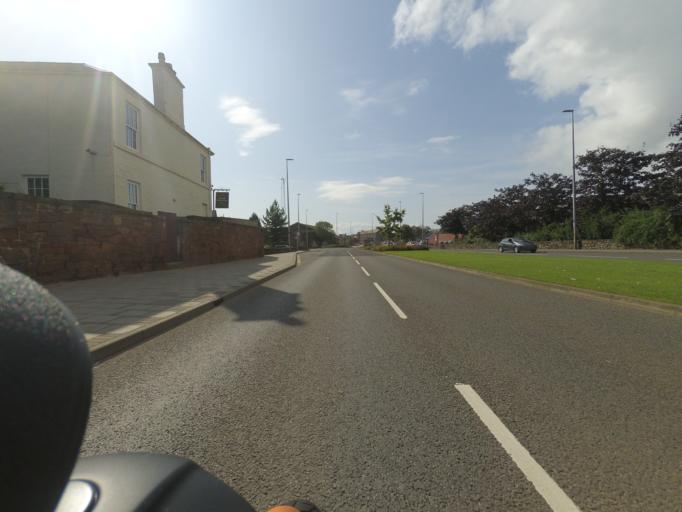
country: GB
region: Scotland
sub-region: Angus
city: Arbroath
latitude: 56.5613
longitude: -2.5857
